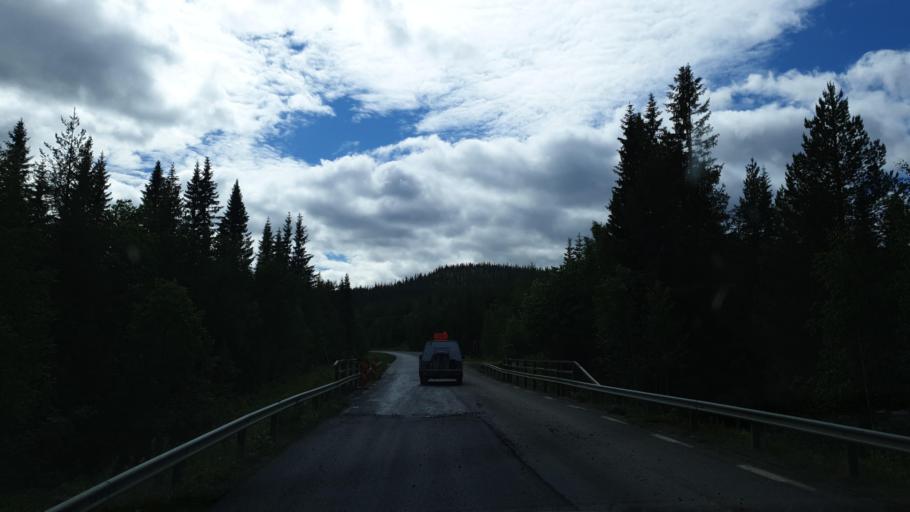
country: SE
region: Vaesterbotten
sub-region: Vilhelmina Kommun
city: Sjoberg
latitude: 64.8985
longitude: 15.8595
